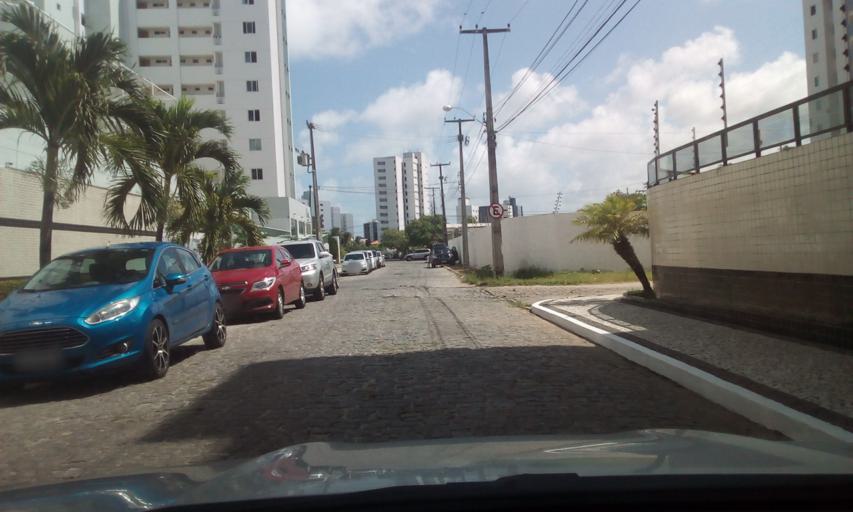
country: BR
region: Paraiba
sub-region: Joao Pessoa
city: Joao Pessoa
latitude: -7.0749
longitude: -34.8349
